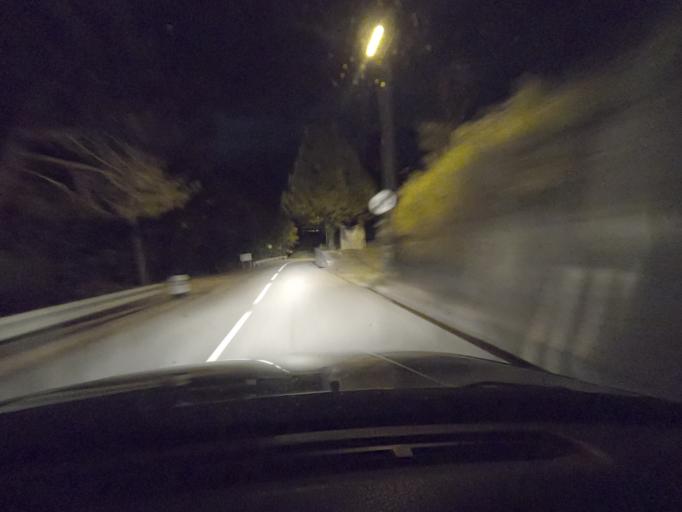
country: PT
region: Vila Real
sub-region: Santa Marta de Penaguiao
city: Santa Marta de Penaguiao
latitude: 41.2234
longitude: -7.8173
